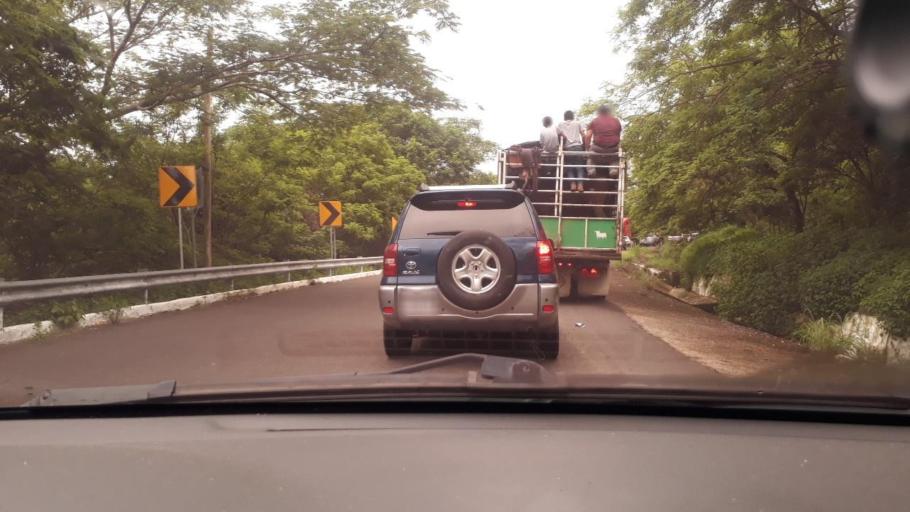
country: GT
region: Jutiapa
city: Jalpatagua
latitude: 14.1663
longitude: -90.0519
